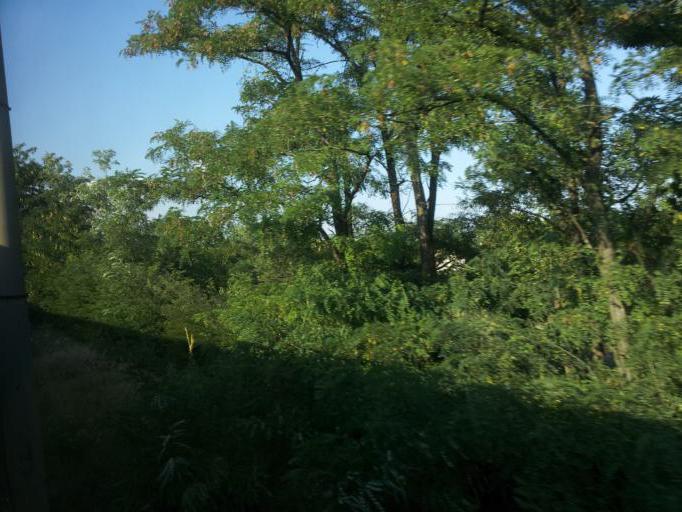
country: HU
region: Pest
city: Dunavarsany
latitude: 47.2833
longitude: 19.0668
